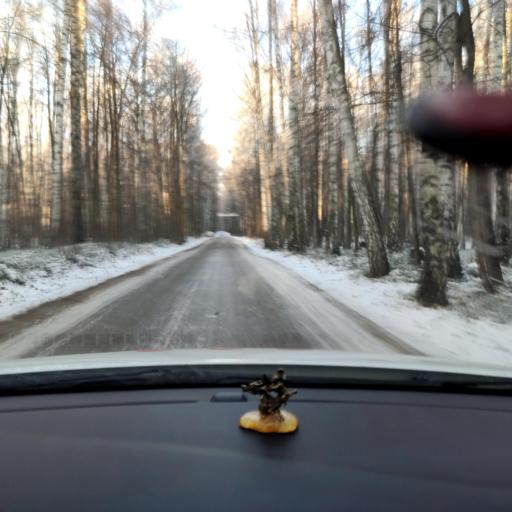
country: RU
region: Tatarstan
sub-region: Gorod Kazan'
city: Kazan
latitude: 55.6761
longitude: 49.1012
